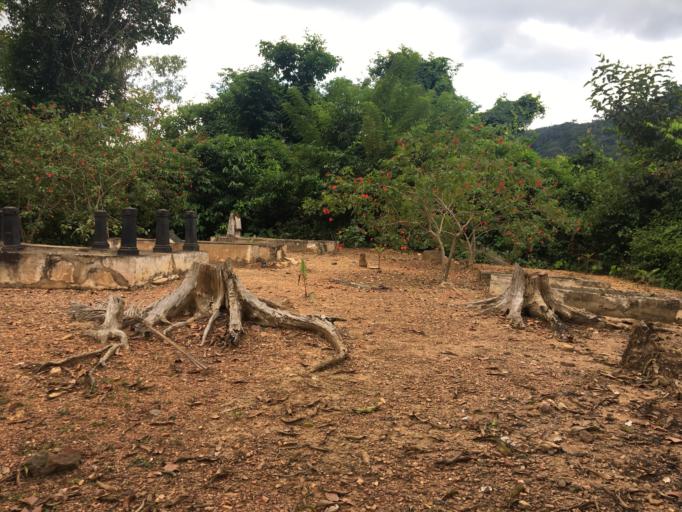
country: TG
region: Plateaux
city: Kpalime
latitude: 6.9449
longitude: 0.5855
